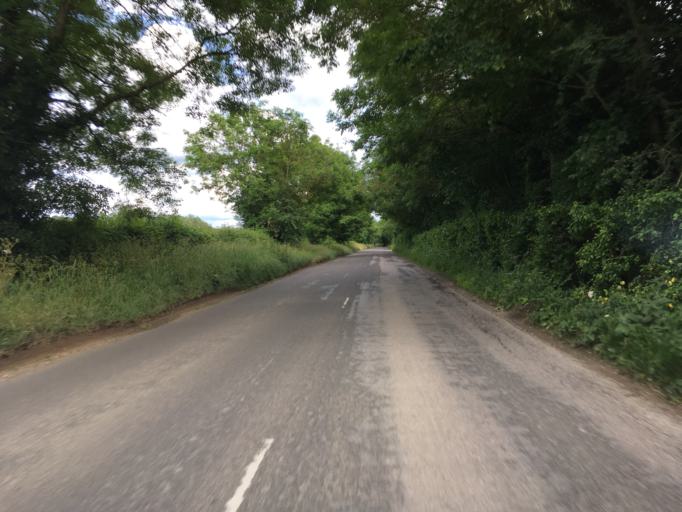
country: GB
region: England
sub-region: Wiltshire
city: Minety
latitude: 51.6557
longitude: -1.9471
